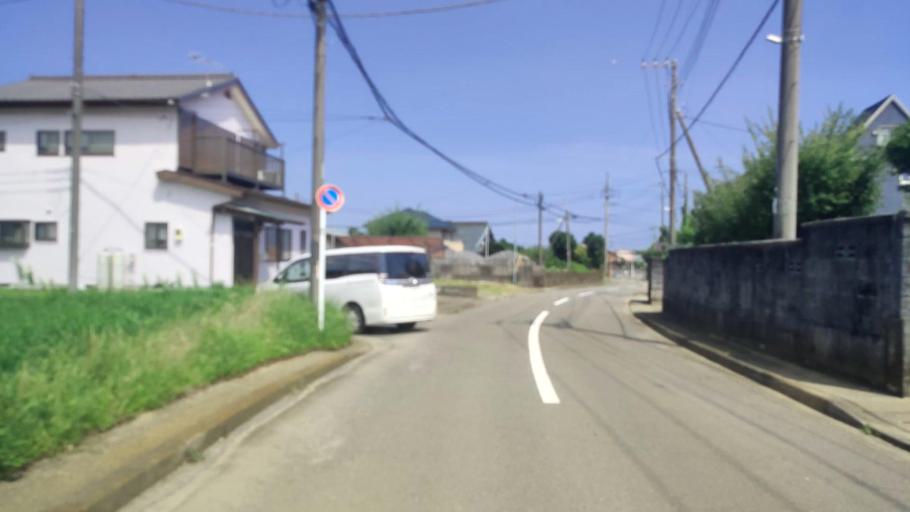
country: JP
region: Kanagawa
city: Hadano
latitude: 35.3571
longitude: 139.2510
